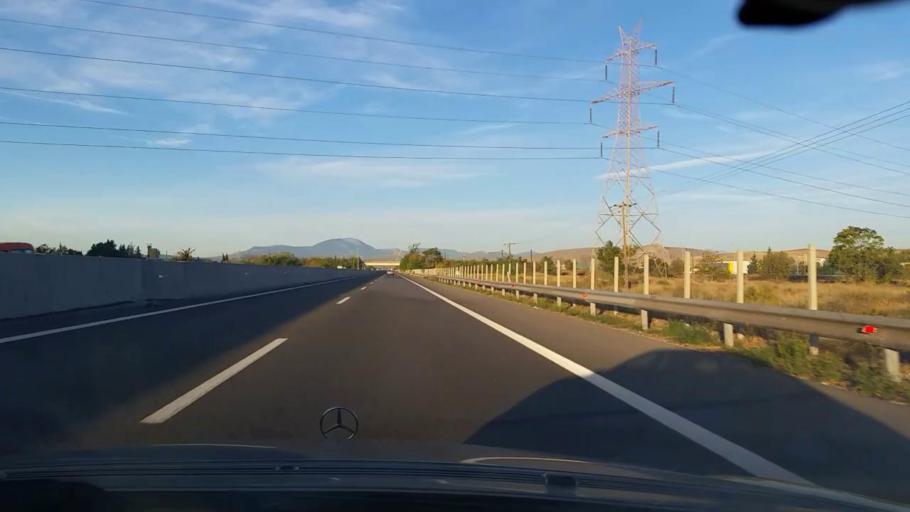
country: GR
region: Central Greece
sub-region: Nomos Voiotias
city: Thivai
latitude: 38.3712
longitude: 23.3905
